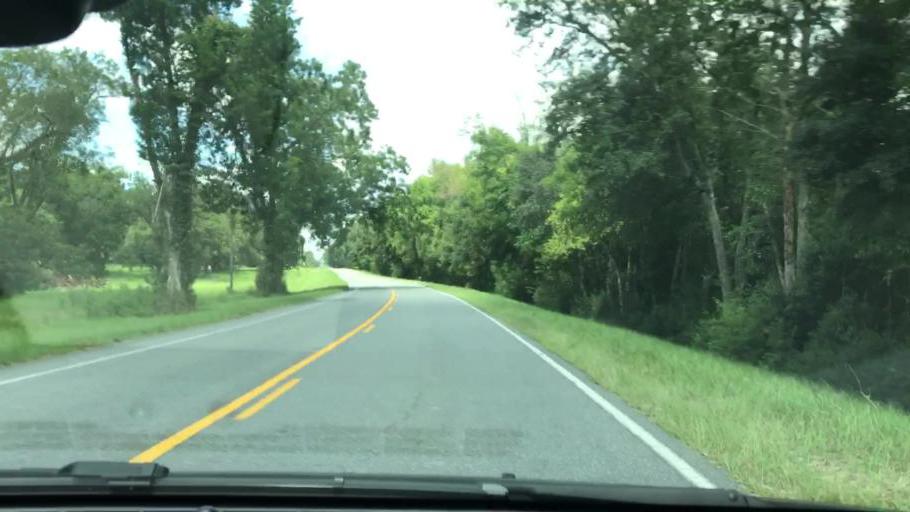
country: US
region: Florida
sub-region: Jackson County
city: Malone
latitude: 30.9110
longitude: -85.1204
